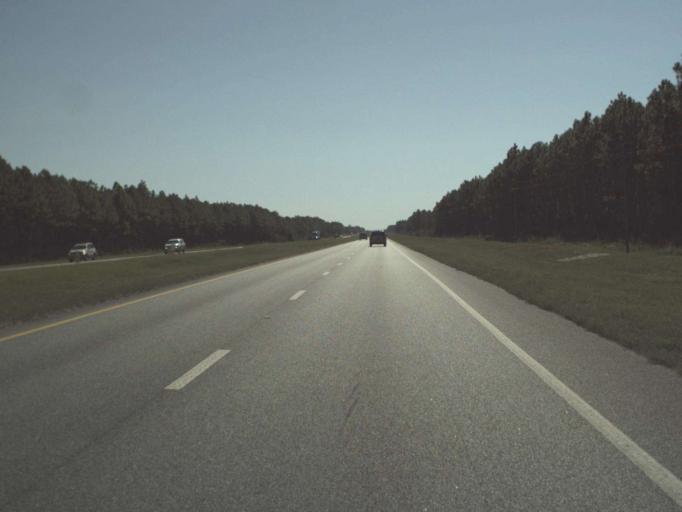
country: US
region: Florida
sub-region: Walton County
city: Seaside
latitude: 30.3084
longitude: -86.0356
